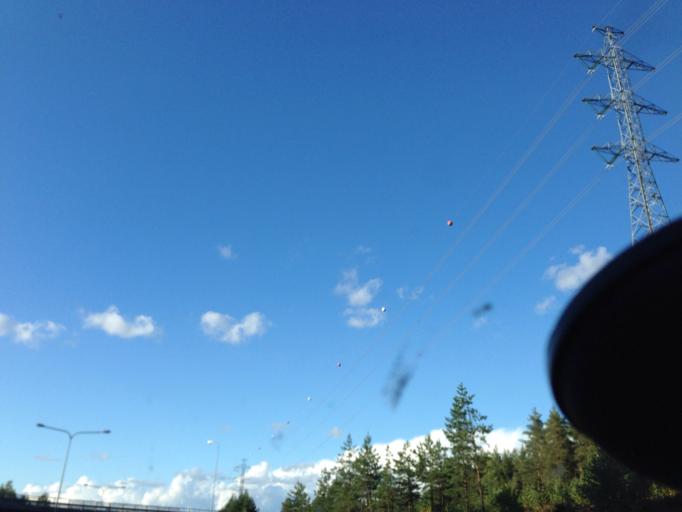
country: FI
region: Uusimaa
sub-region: Helsinki
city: Vantaa
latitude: 60.3167
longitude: 24.9973
